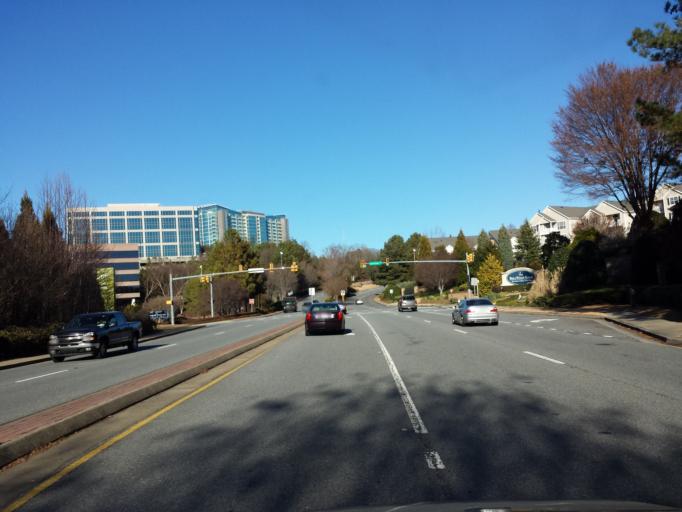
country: US
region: Georgia
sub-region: Cobb County
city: Vinings
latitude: 33.8988
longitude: -84.4590
